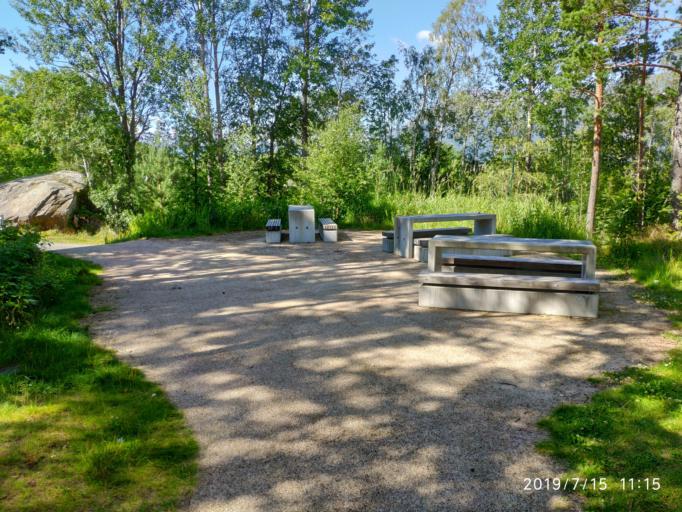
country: NO
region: Hordaland
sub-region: Granvin
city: Granvin
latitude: 60.4706
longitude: 6.8341
